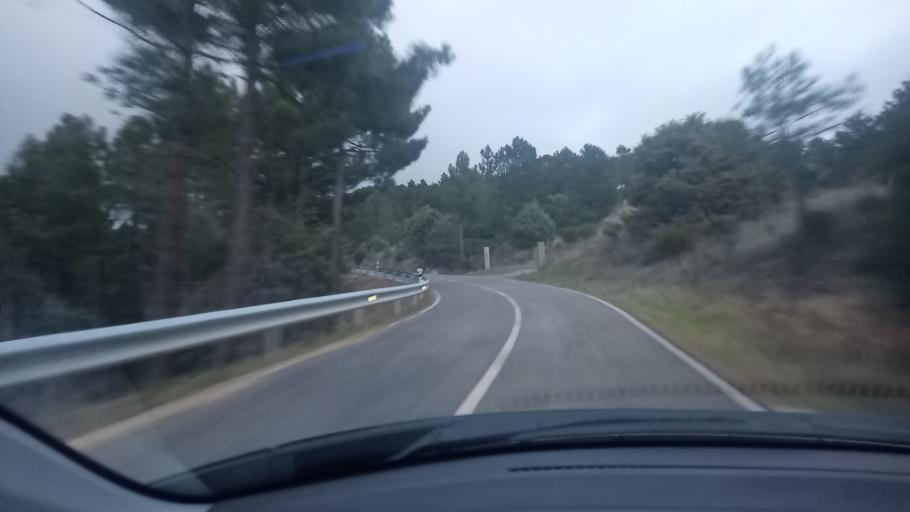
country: ES
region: Madrid
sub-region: Provincia de Madrid
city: Zarzalejo
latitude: 40.5525
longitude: -4.1950
